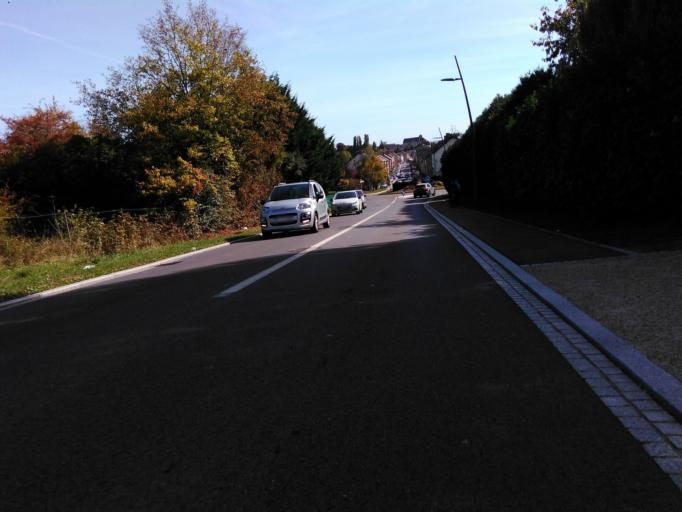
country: FR
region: Lorraine
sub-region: Departement de la Moselle
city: Hettange-Grande
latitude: 49.4132
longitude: 6.1431
